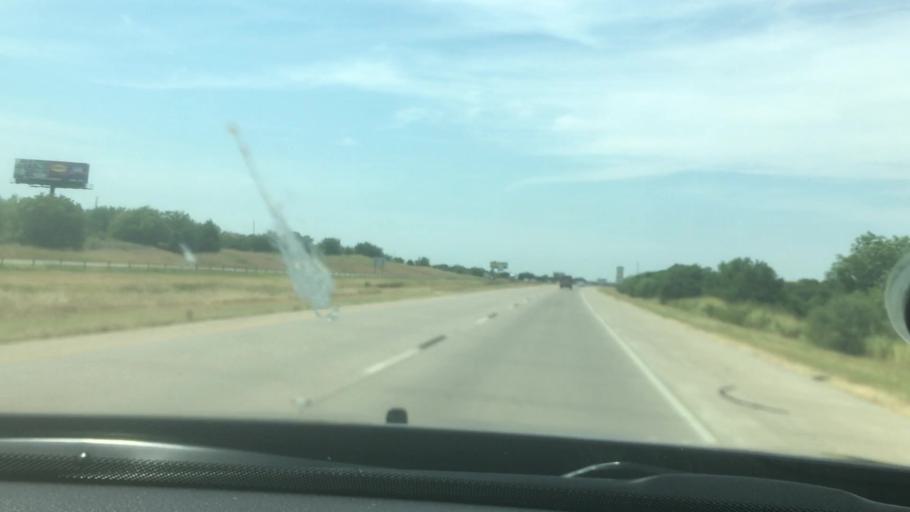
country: US
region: Oklahoma
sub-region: Carter County
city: Ardmore
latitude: 34.2951
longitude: -97.1595
